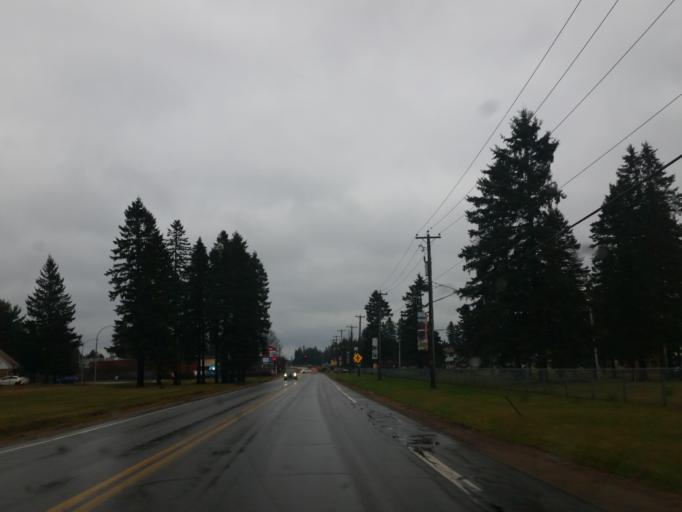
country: CA
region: Quebec
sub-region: Capitale-Nationale
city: Shannon
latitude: 46.8873
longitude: -71.5129
